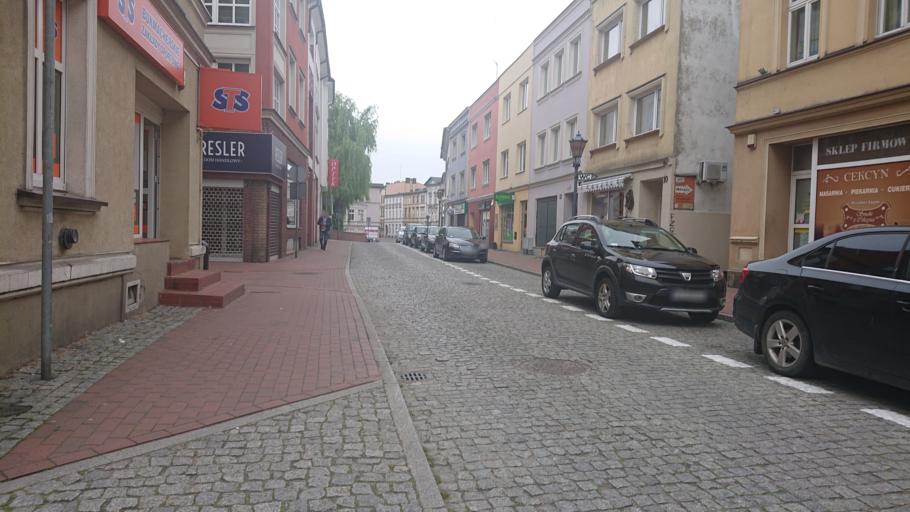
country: PL
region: Pomeranian Voivodeship
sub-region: Powiat chojnicki
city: Chojnice
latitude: 53.6960
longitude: 17.5604
